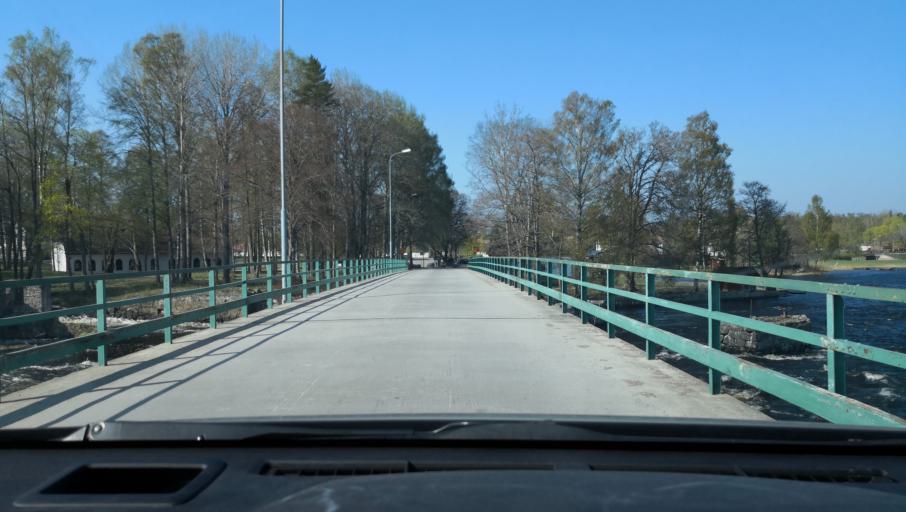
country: SE
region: Uppsala
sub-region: Heby Kommun
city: Tarnsjo
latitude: 60.2861
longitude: 16.8843
